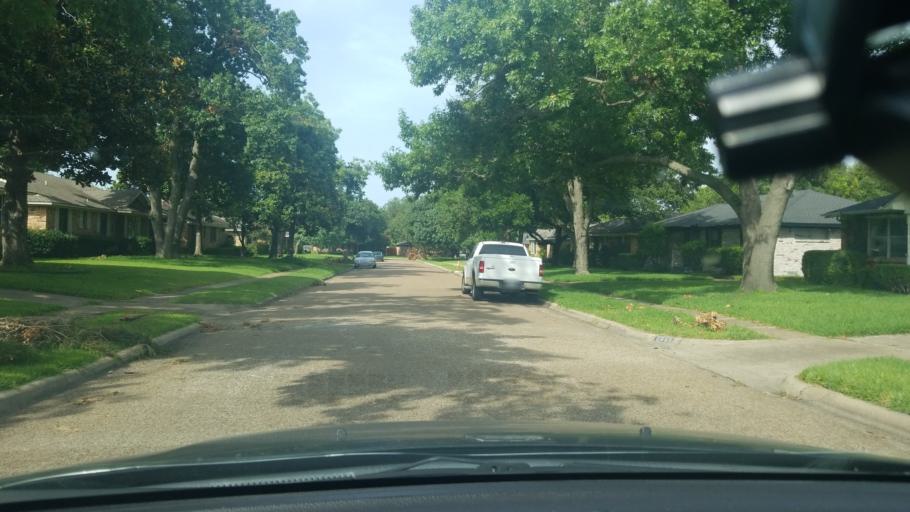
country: US
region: Texas
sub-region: Dallas County
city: Highland Park
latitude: 32.8040
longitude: -96.7000
